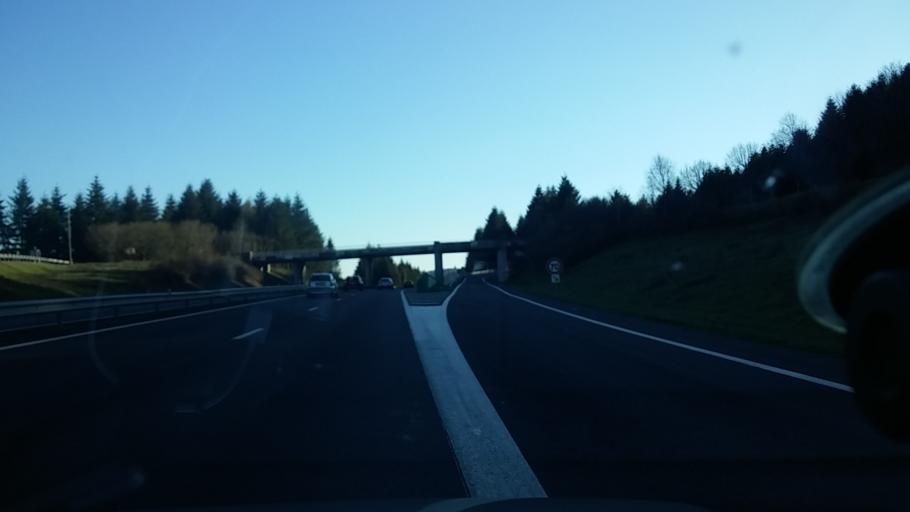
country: FR
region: Limousin
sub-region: Departement de la Haute-Vienne
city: Razes
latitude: 46.0268
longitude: 1.3457
